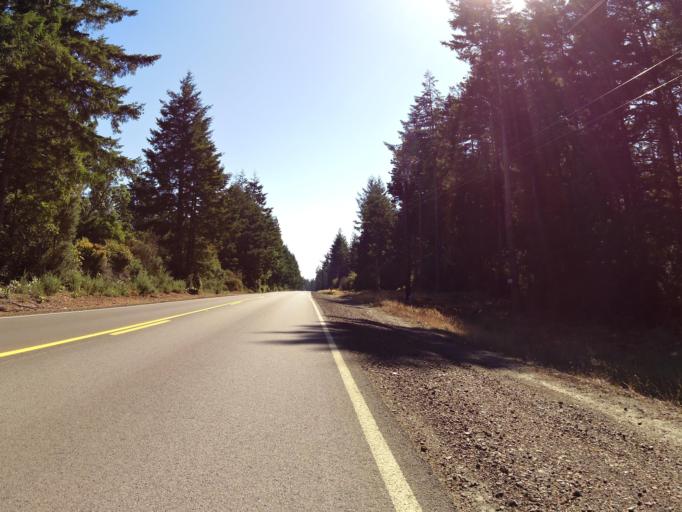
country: US
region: Oregon
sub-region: Coos County
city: Bandon
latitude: 43.2018
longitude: -124.3661
